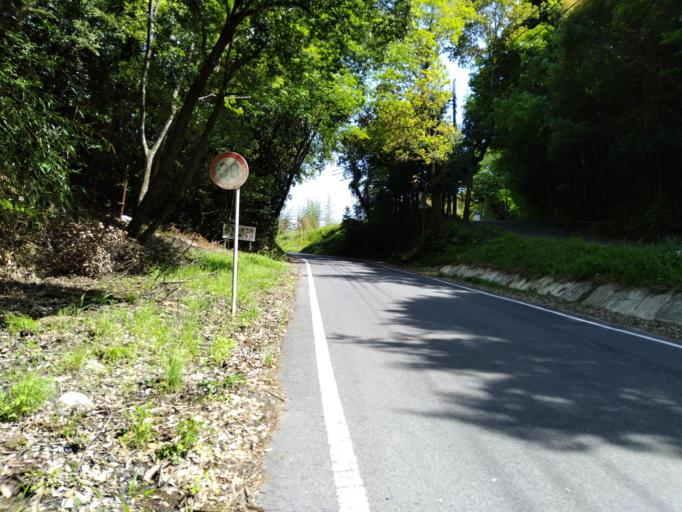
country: JP
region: Gifu
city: Toki
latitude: 35.2463
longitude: 137.2345
